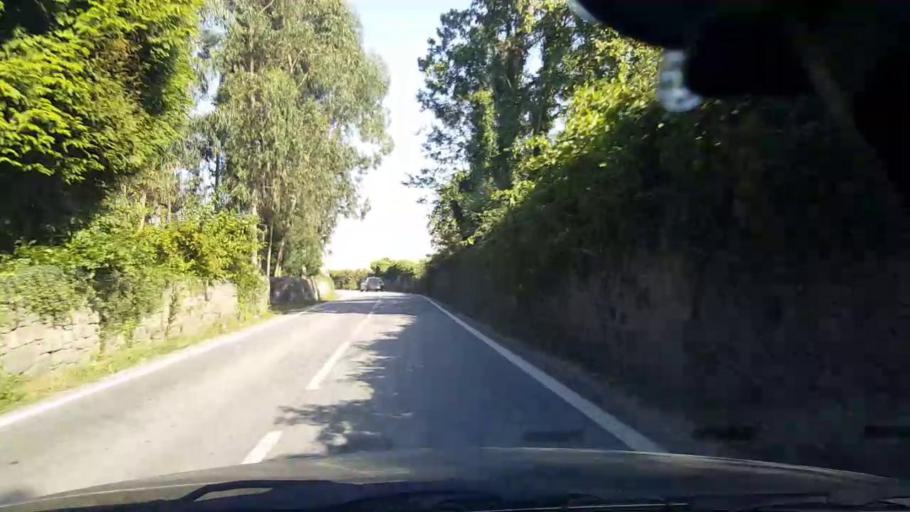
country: PT
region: Porto
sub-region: Vila do Conde
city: Arvore
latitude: 41.3200
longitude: -8.6796
